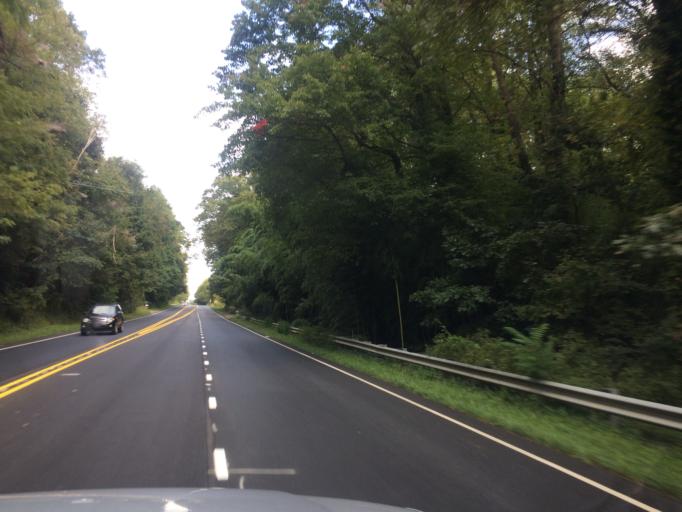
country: US
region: North Carolina
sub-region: Haywood County
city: Canton
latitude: 35.5392
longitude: -82.7642
